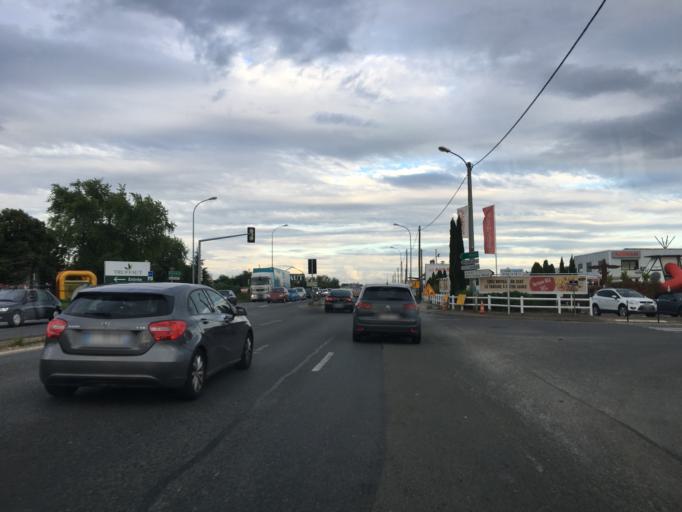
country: FR
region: Ile-de-France
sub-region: Departement de Seine-et-Marne
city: Servon
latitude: 48.7116
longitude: 2.5809
